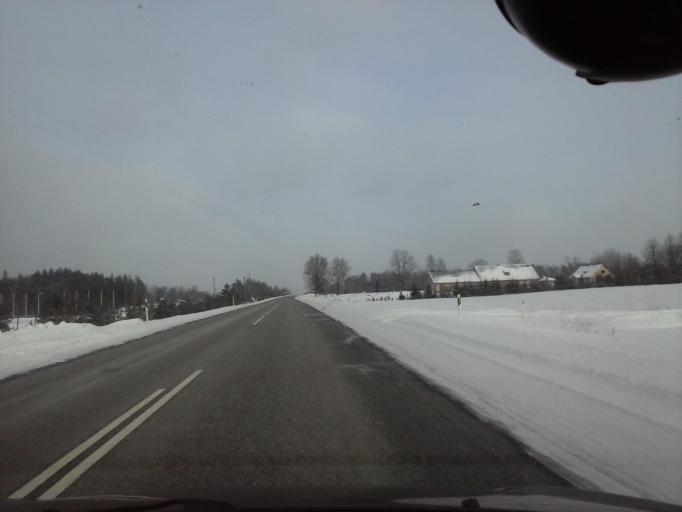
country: EE
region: Paernumaa
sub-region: Saarde vald
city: Kilingi-Nomme
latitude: 58.1659
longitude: 25.0176
